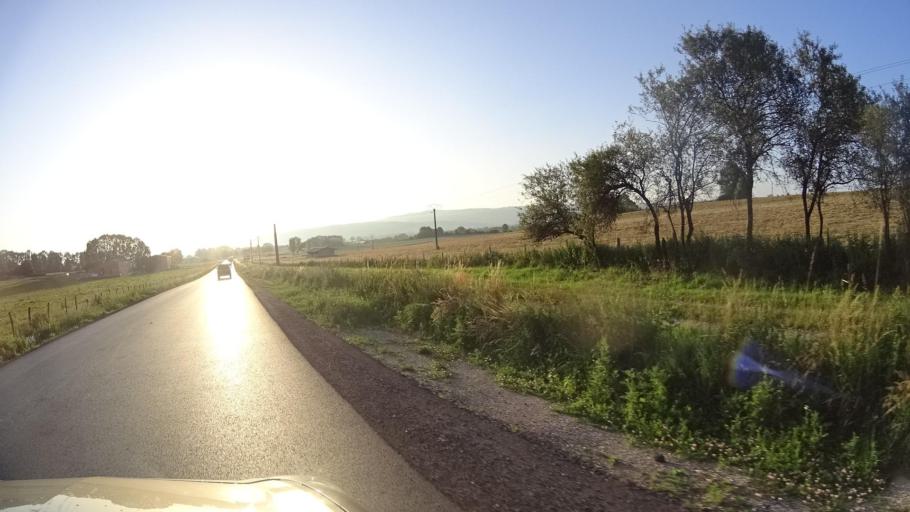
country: FR
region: Franche-Comte
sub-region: Departement du Doubs
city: Doubs
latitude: 46.9175
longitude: 6.2914
